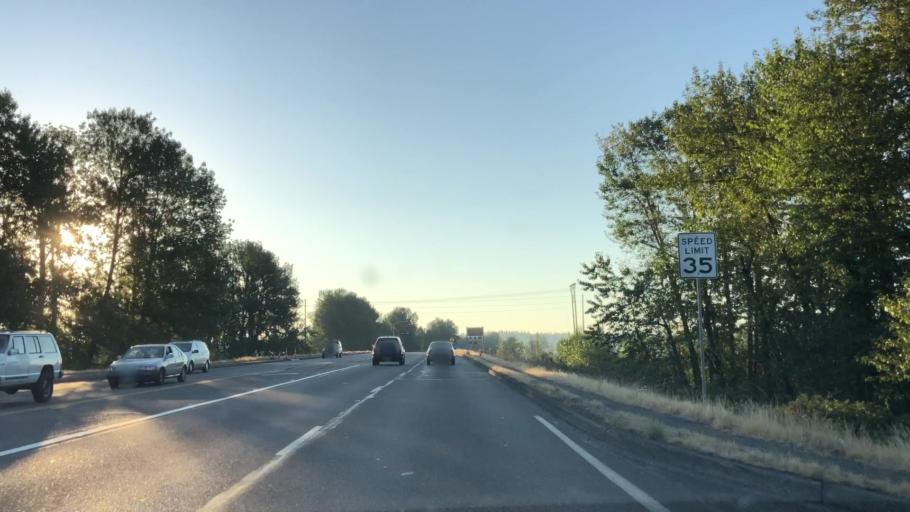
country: US
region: Washington
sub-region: King County
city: Auburn
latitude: 47.3222
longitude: -122.2424
